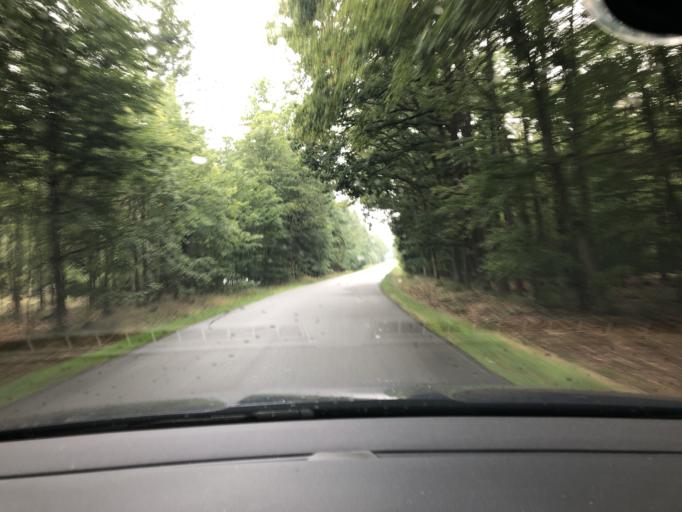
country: CZ
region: South Moravian
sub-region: Okres Znojmo
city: Jevisovice
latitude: 49.0266
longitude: 15.9502
